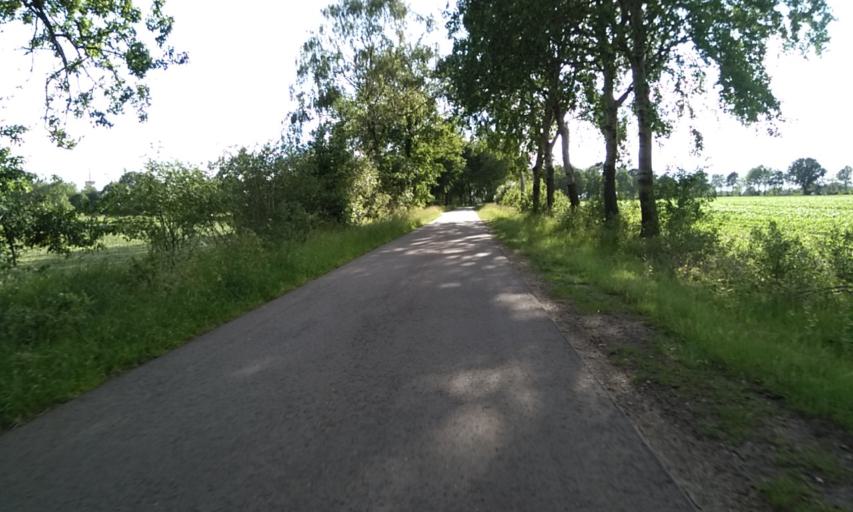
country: DE
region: Lower Saxony
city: Ahlerstedt
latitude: 53.3613
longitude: 9.4407
